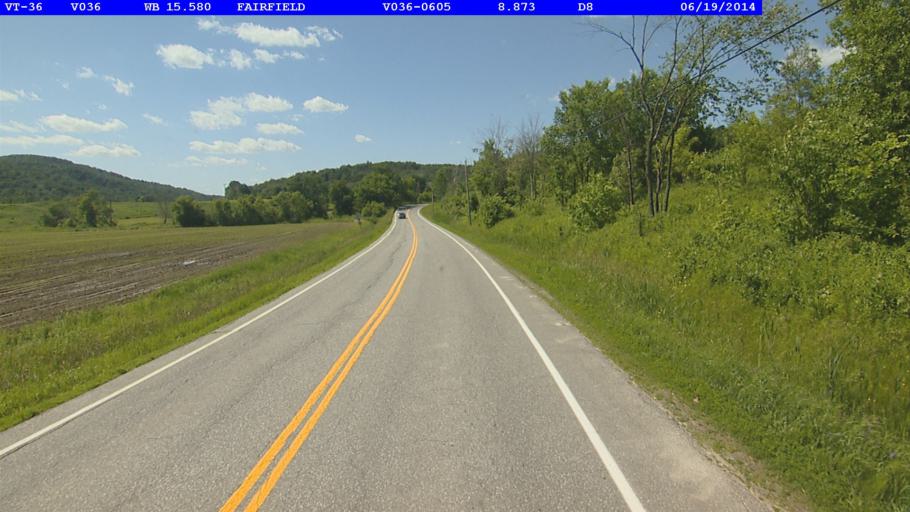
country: US
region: Vermont
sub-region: Franklin County
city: Enosburg Falls
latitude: 44.7899
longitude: -72.8685
